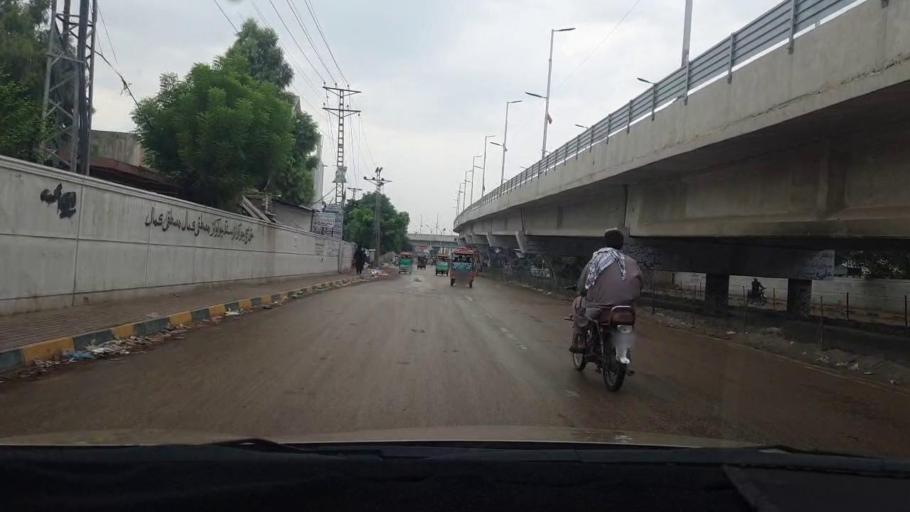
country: PK
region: Sindh
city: Larkana
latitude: 27.5625
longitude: 68.2051
